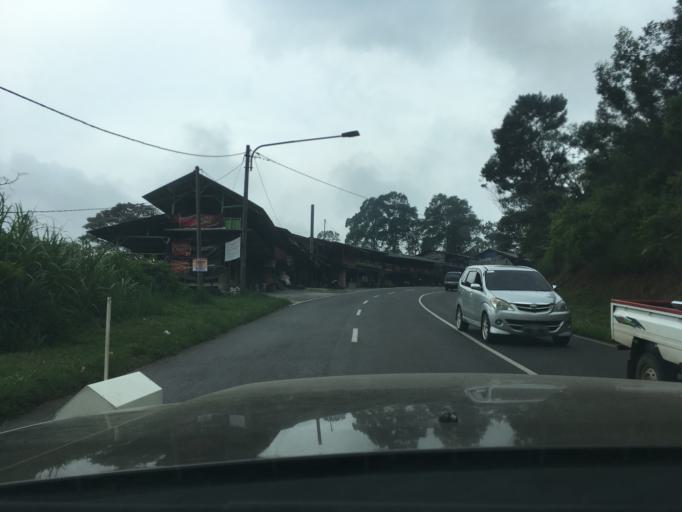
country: ID
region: West Java
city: Lembang
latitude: -6.7703
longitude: 107.6365
